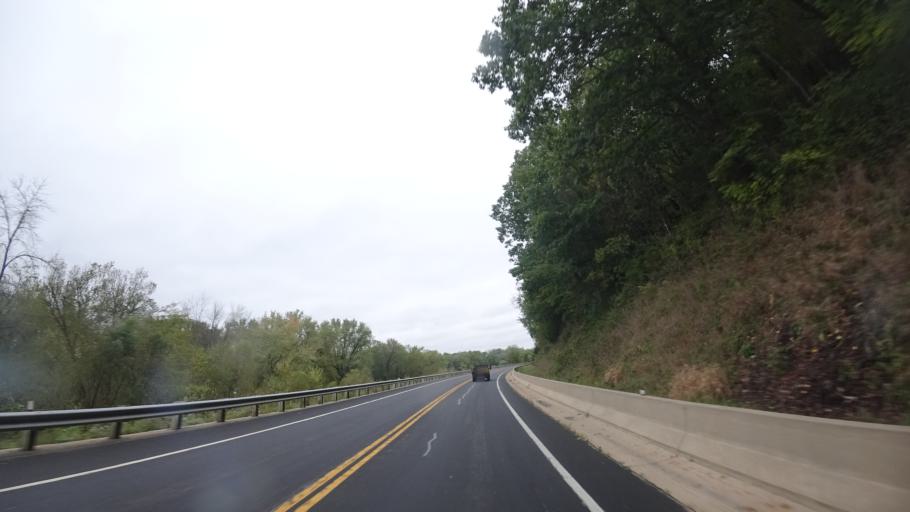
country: US
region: Wisconsin
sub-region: Grant County
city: Boscobel
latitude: 43.1406
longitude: -90.7359
